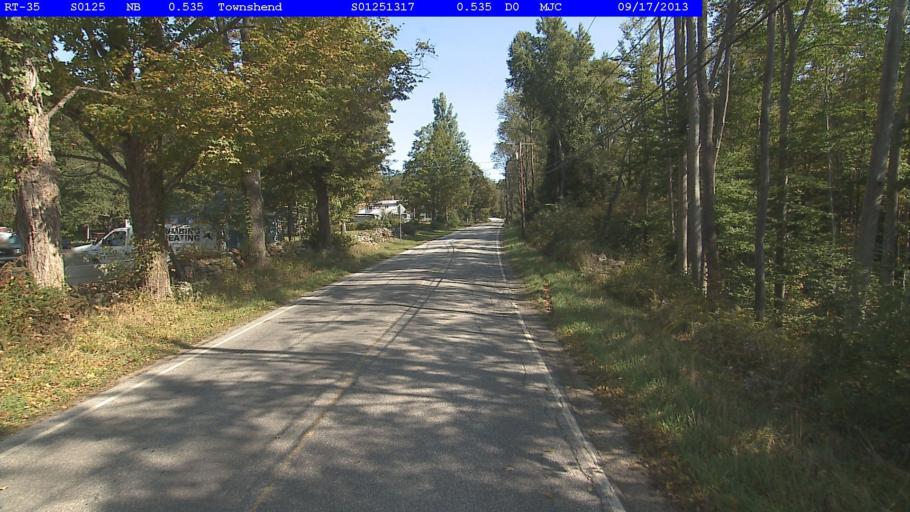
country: US
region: Vermont
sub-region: Windham County
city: Newfane
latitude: 43.0536
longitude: -72.6654
